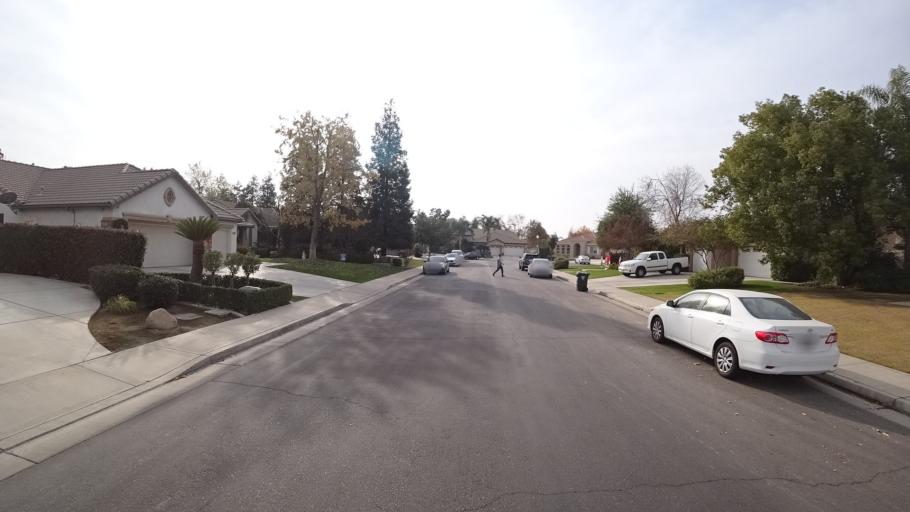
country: US
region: California
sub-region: Kern County
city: Rosedale
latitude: 35.3441
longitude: -119.1380
